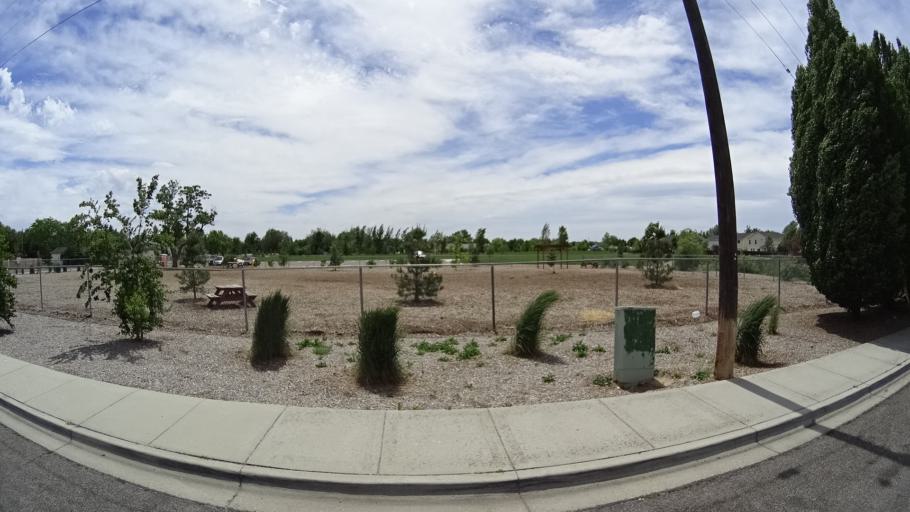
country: US
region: Idaho
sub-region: Ada County
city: Garden City
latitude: 43.6158
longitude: -116.3055
